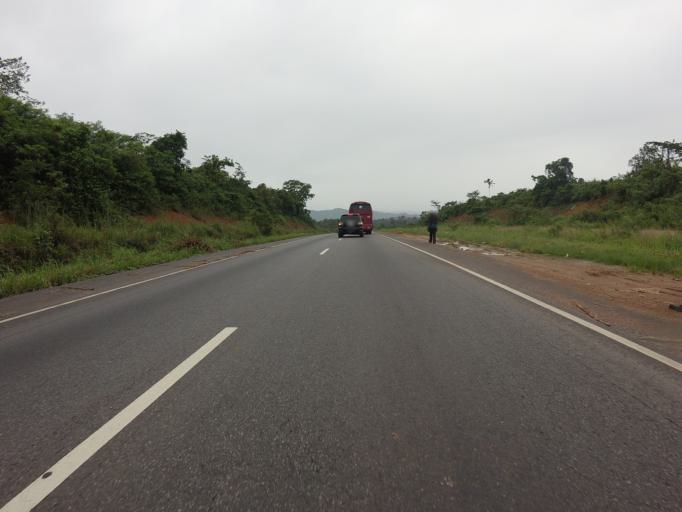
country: GH
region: Eastern
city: Suhum
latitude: 6.0776
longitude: -0.4719
